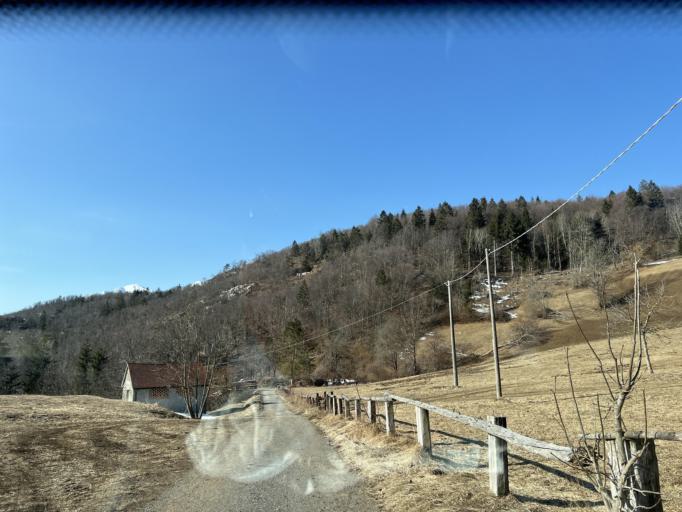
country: IT
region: Friuli Venezia Giulia
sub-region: Provincia di Udine
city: Chiaulis
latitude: 46.4199
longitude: 12.9771
